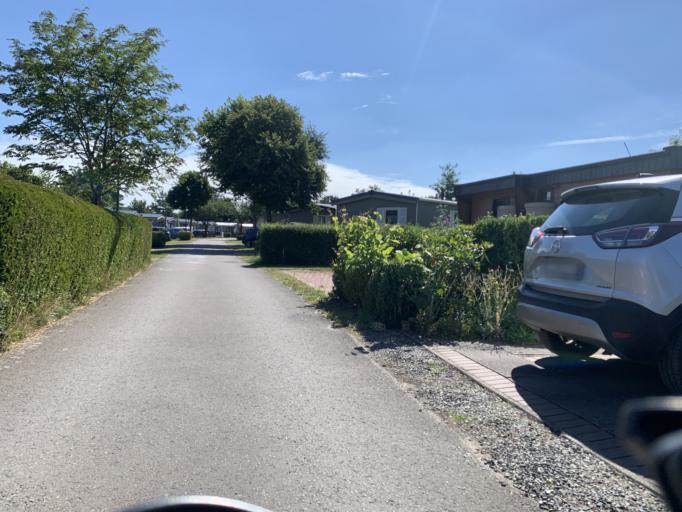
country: DE
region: Lower Saxony
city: Wietzendorf
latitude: 52.9373
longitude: 9.9708
